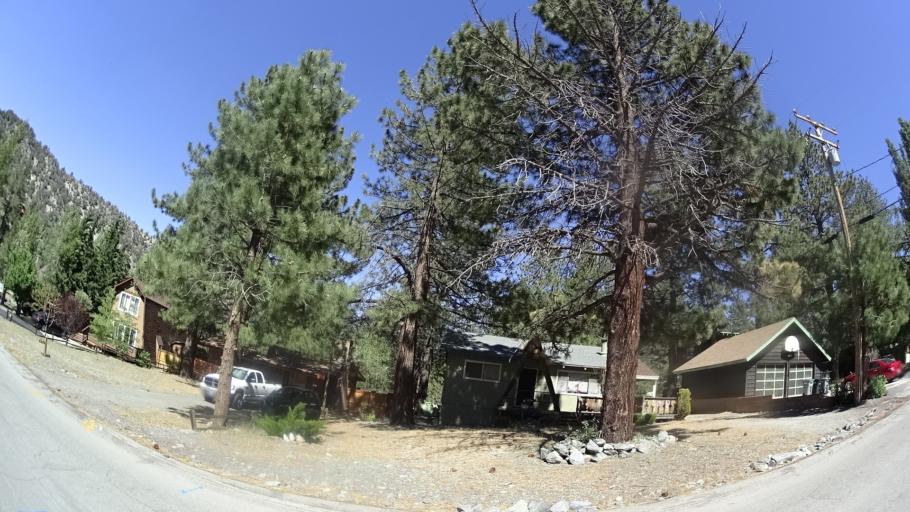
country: US
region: California
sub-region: San Bernardino County
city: Wrightwood
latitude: 34.3647
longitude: -117.6522
